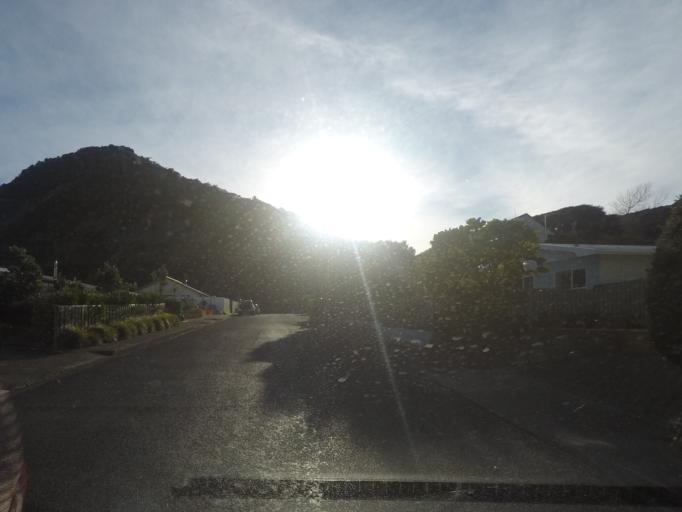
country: NZ
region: Tasman
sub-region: Tasman District
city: Takaka
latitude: -40.8100
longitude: 172.9169
